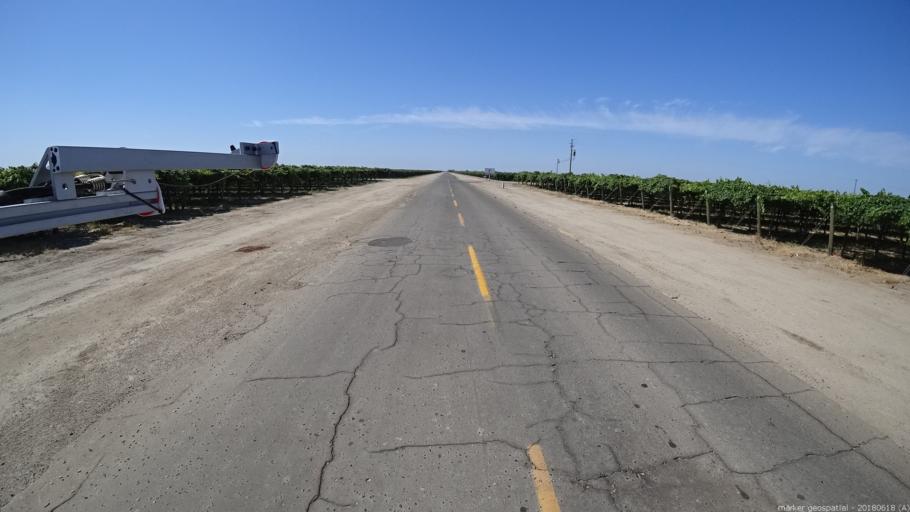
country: US
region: California
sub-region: Fresno County
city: Mendota
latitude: 36.8300
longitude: -120.2591
